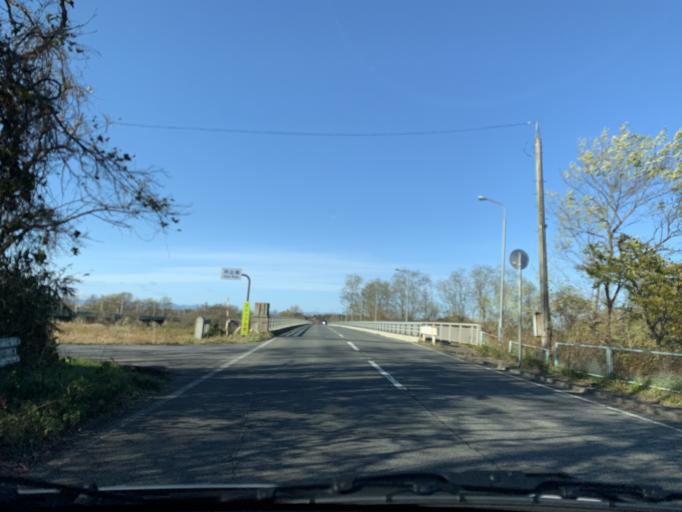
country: JP
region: Iwate
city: Mizusawa
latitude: 39.1850
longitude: 141.1281
